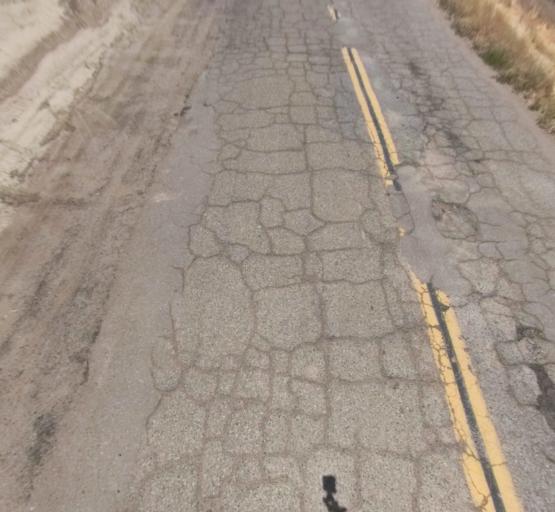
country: US
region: California
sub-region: Madera County
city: Chowchilla
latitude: 37.0843
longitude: -120.3470
